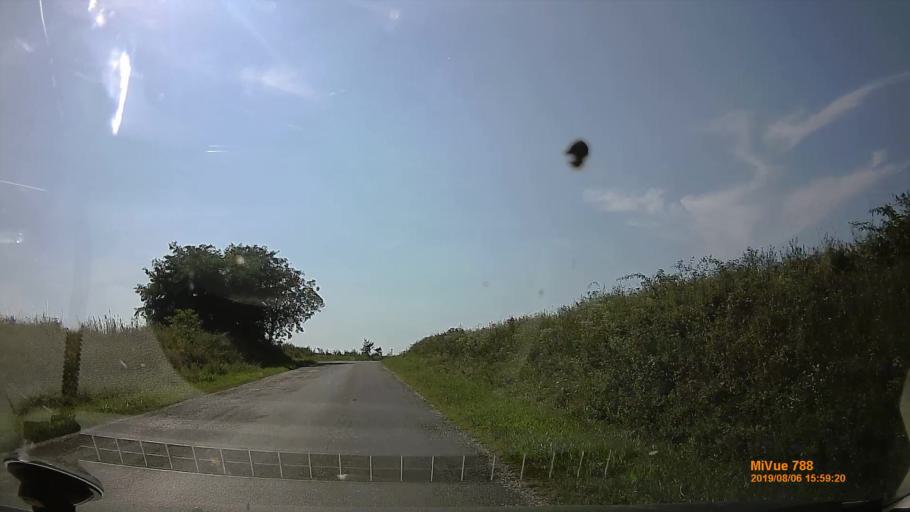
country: HU
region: Somogy
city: Csurgo
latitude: 46.2940
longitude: 16.9932
